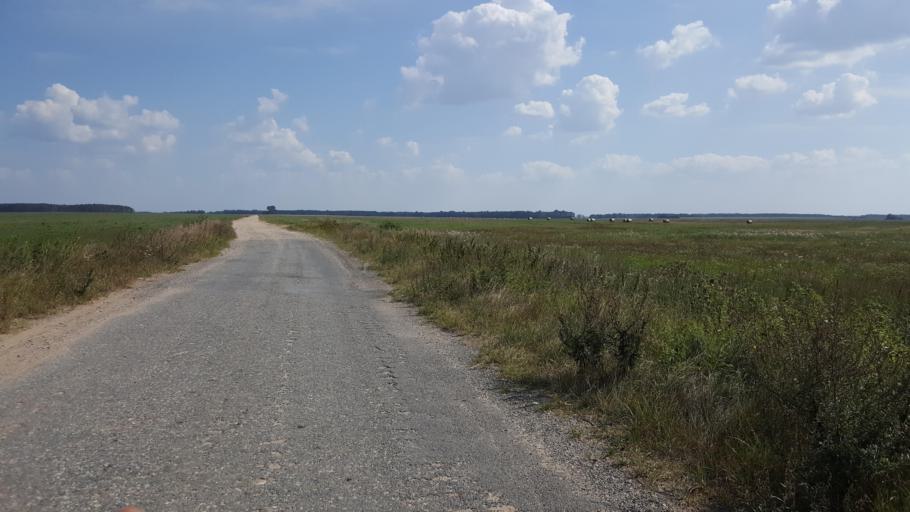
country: BY
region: Brest
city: Kamyanyuki
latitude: 52.4916
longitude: 23.5876
